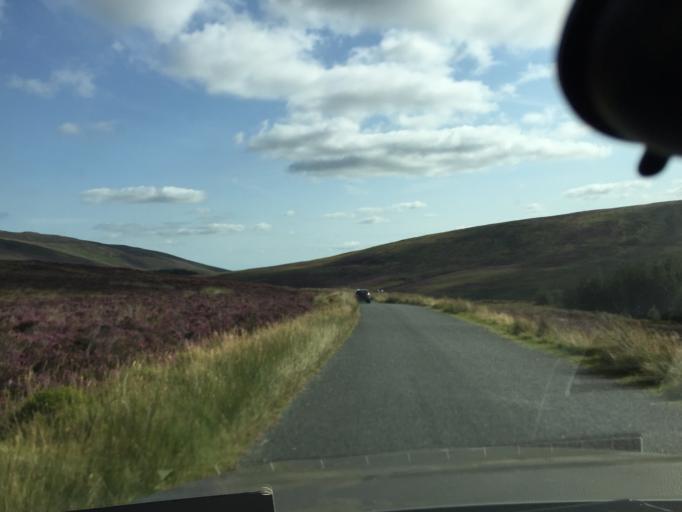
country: IE
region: Leinster
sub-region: Wicklow
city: Rathdrum
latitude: 53.0745
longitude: -6.3530
